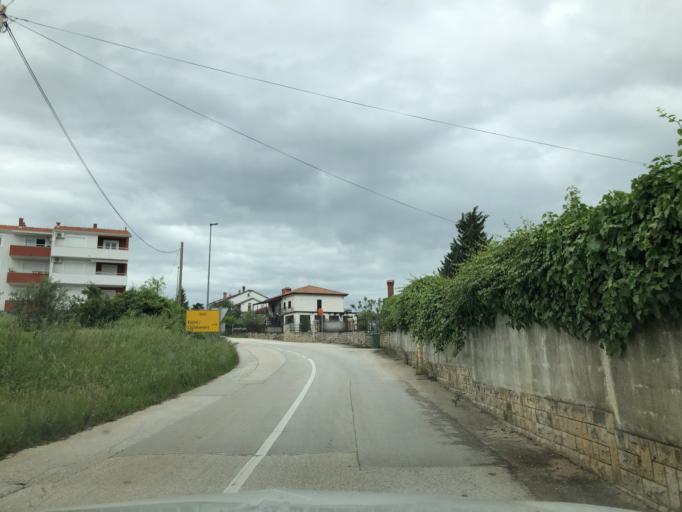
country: HR
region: Istarska
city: Buje
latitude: 45.4502
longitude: 13.6367
